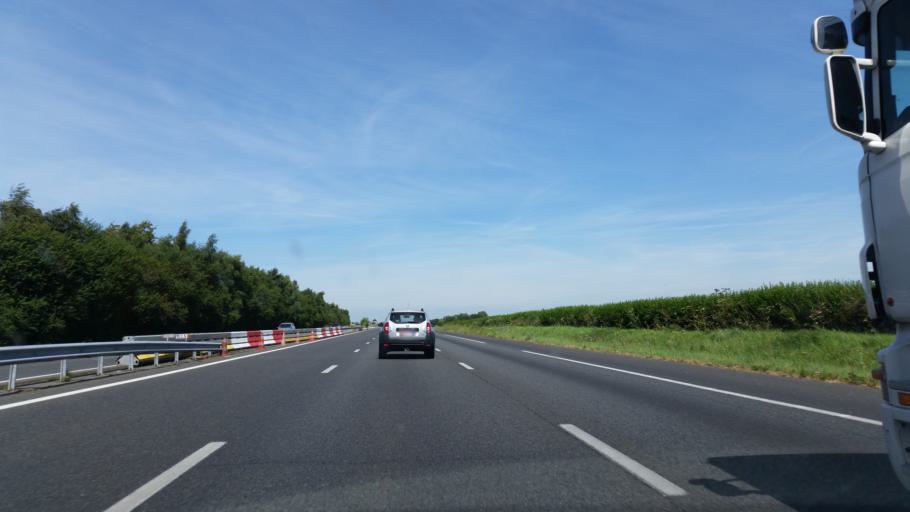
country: FR
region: Nord-Pas-de-Calais
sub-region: Departement du Pas-de-Calais
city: Vaulx-Vraucourt
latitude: 50.1603
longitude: 2.8737
